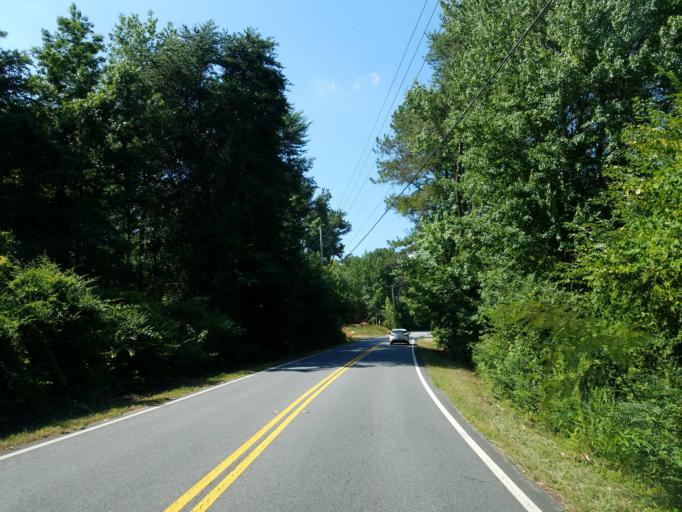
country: US
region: Georgia
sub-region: Fulton County
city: Roswell
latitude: 34.0532
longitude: -84.4359
